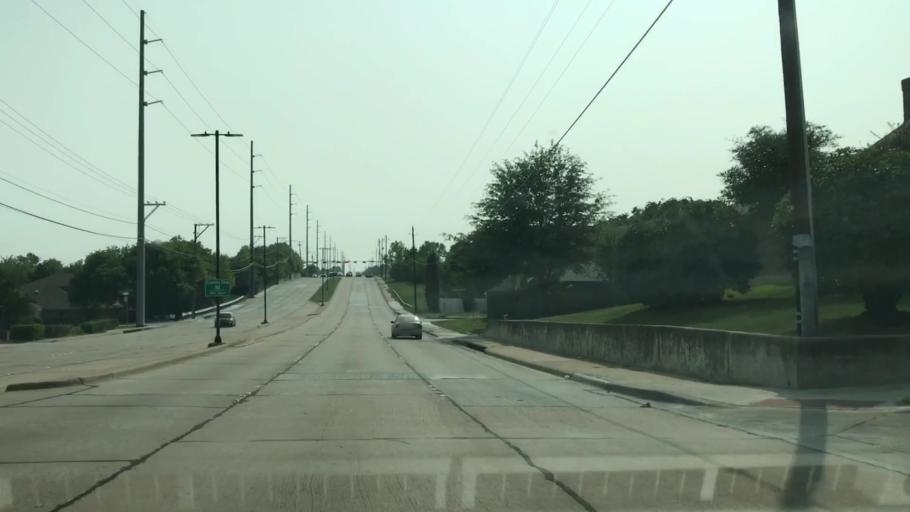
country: US
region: Texas
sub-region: Dallas County
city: Garland
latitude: 32.8890
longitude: -96.6090
